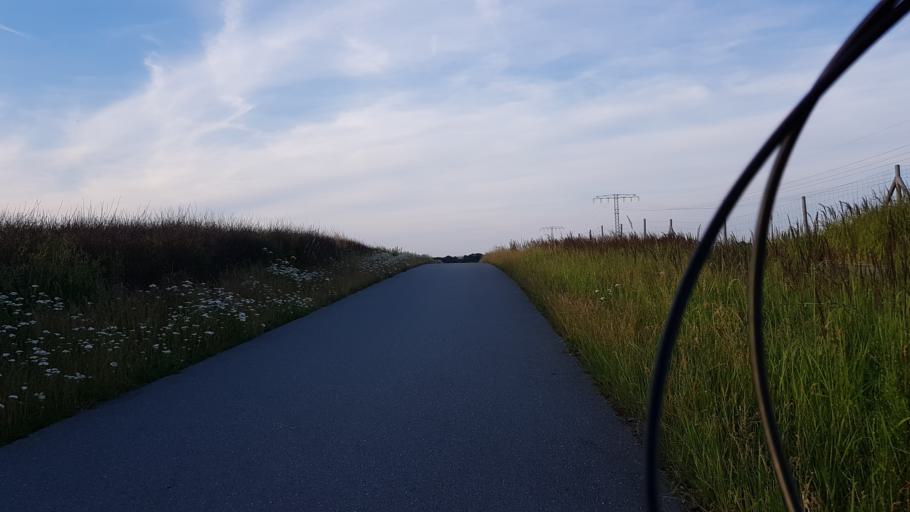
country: DE
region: Mecklenburg-Vorpommern
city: Lankow
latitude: 53.6570
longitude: 11.3526
